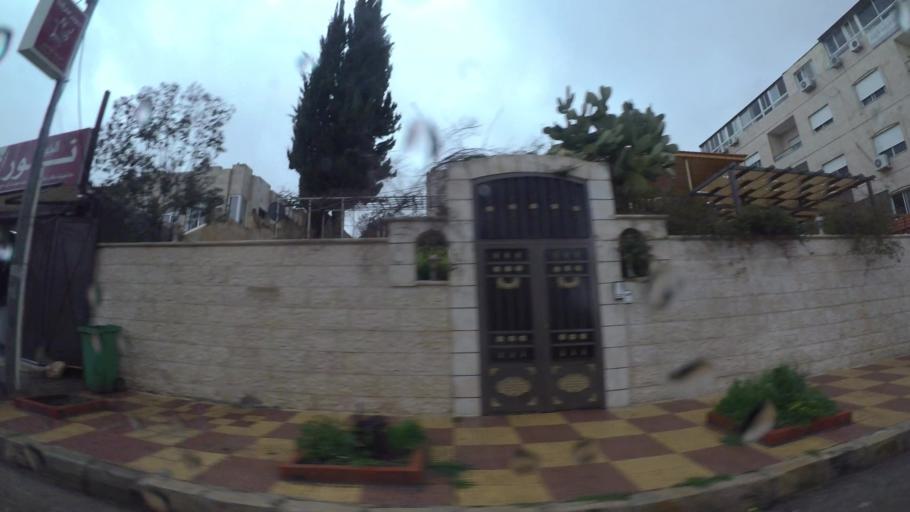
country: JO
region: Amman
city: Al Jubayhah
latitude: 32.0357
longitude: 35.8706
